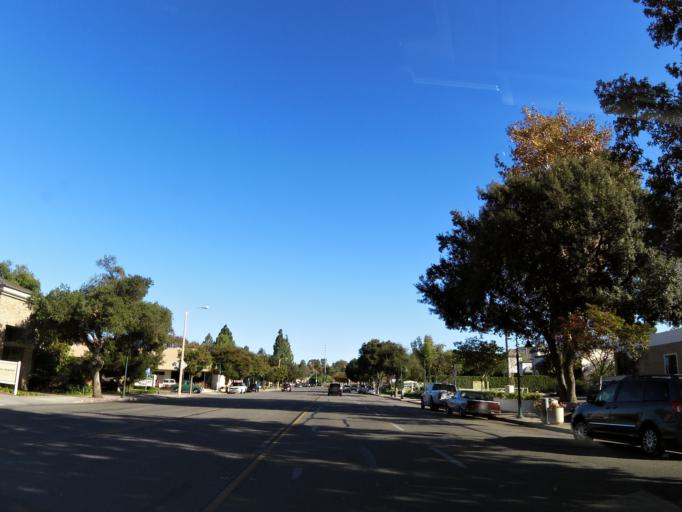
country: US
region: California
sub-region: Ventura County
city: Thousand Oaks
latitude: 34.1790
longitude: -118.8716
